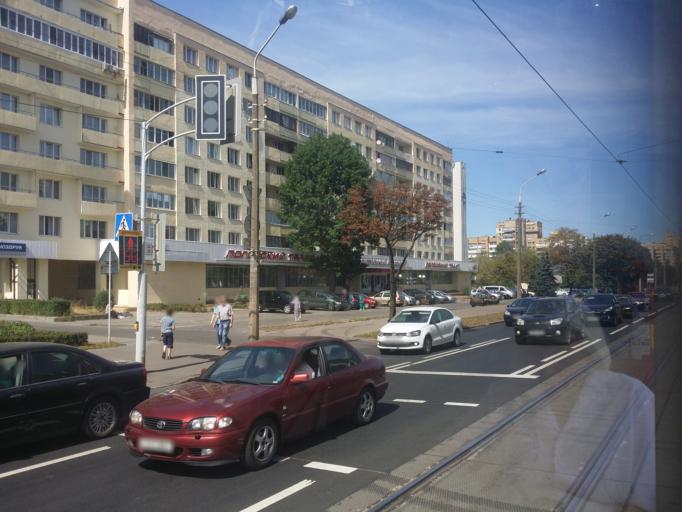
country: BY
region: Minsk
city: Minsk
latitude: 53.9363
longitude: 27.6034
